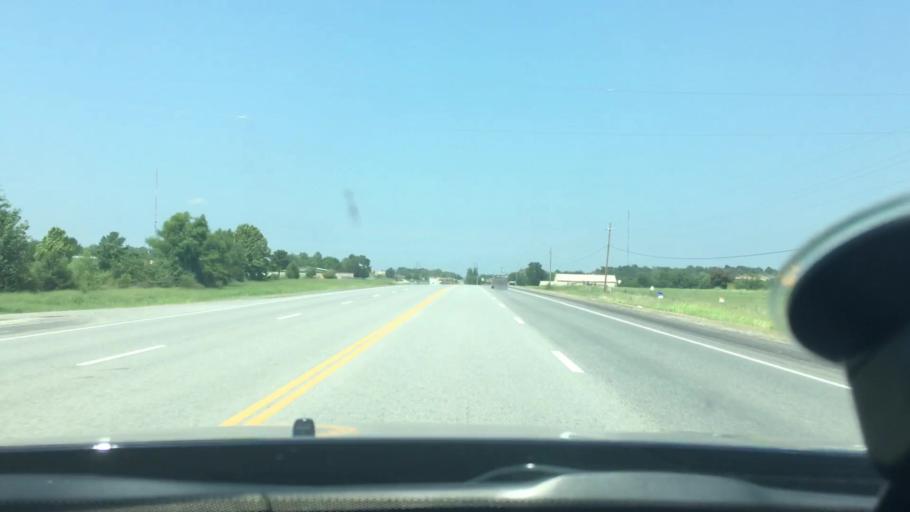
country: US
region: Oklahoma
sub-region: Atoka County
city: Atoka
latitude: 34.3674
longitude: -96.1028
